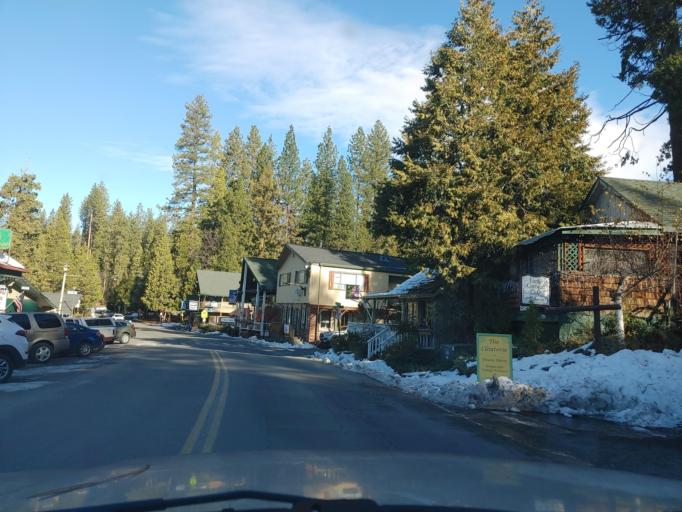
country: US
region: California
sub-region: Tuolumne County
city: Twain Harte
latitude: 38.0385
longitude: -120.2297
